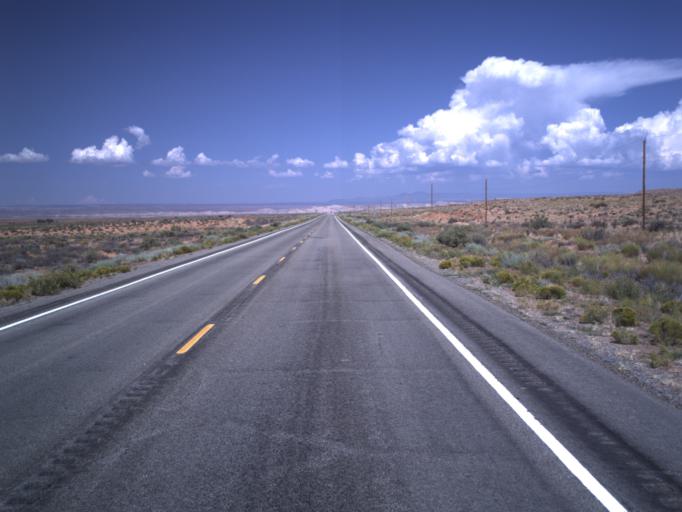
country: US
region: Utah
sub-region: San Juan County
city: Blanding
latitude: 37.1356
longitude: -109.5546
